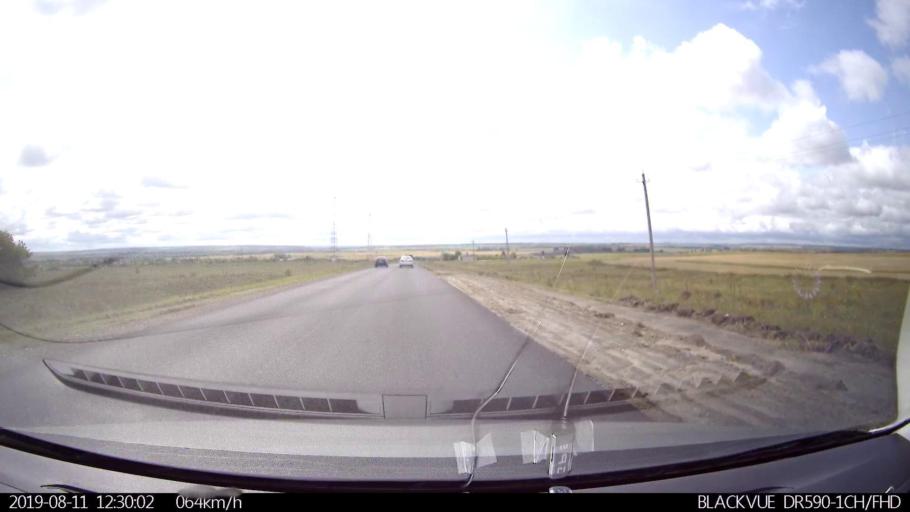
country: RU
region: Ulyanovsk
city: Ignatovka
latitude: 53.8293
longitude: 47.8976
